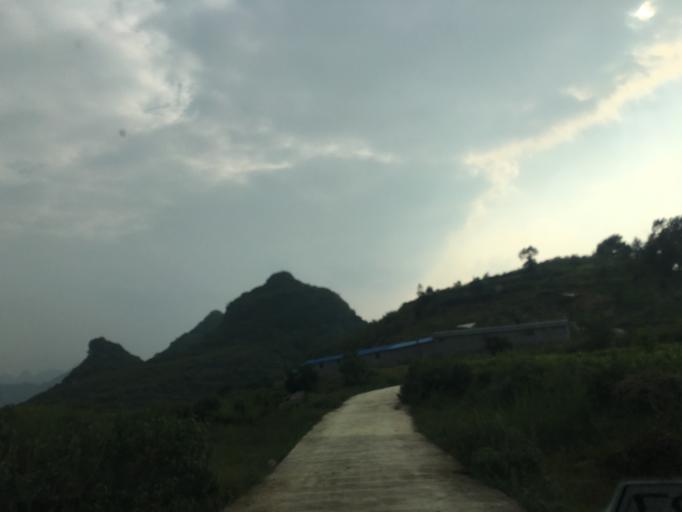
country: CN
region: Guangxi Zhuangzu Zizhiqu
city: Xinzhou
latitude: 25.4390
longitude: 105.6395
